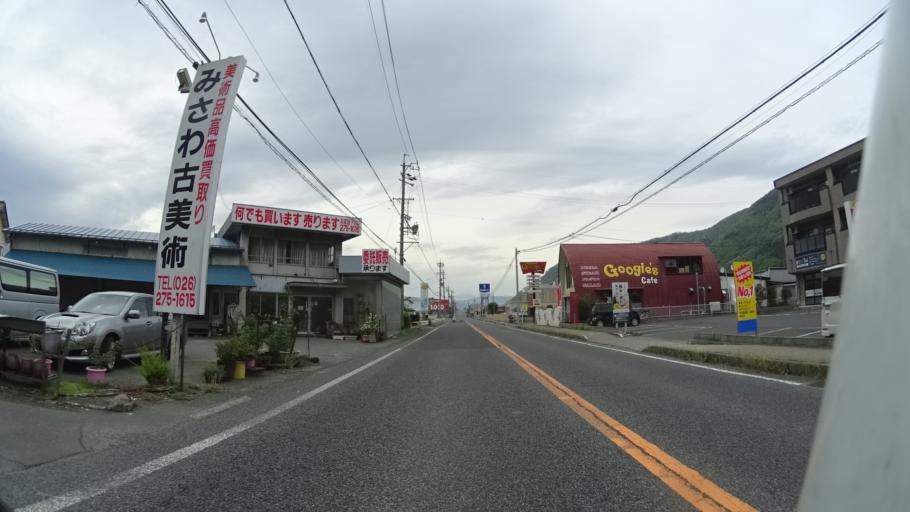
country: JP
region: Nagano
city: Nagano-shi
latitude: 36.4995
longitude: 138.1471
